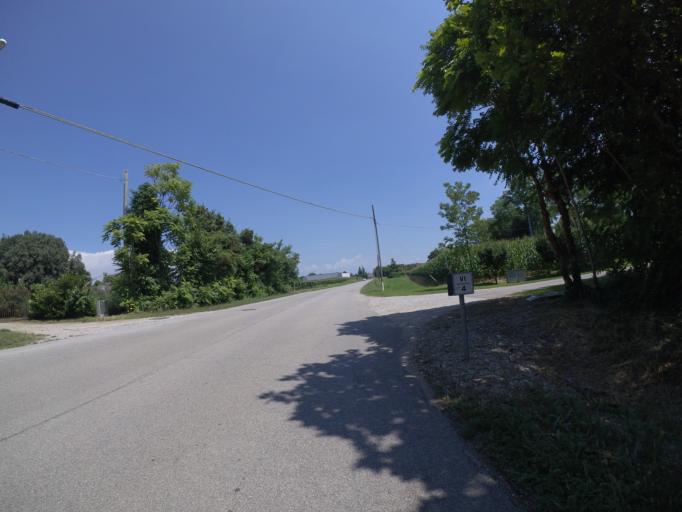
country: IT
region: Friuli Venezia Giulia
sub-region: Provincia di Udine
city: Bertiolo
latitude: 45.9763
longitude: 13.0776
